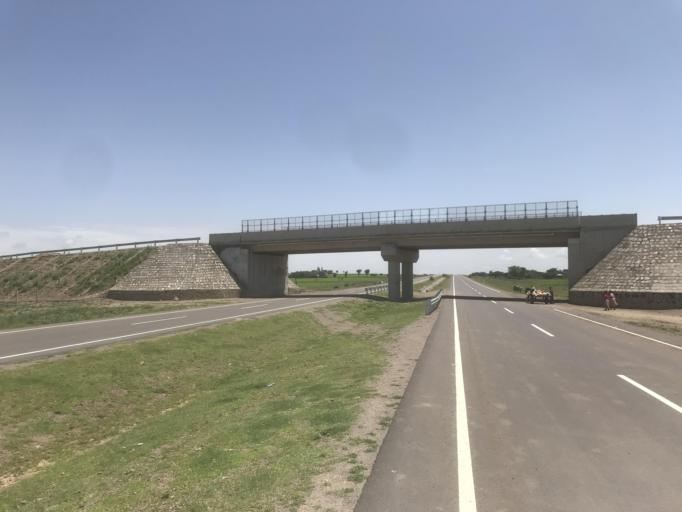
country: ET
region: Oromiya
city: Mojo
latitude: 8.3263
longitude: 38.9591
